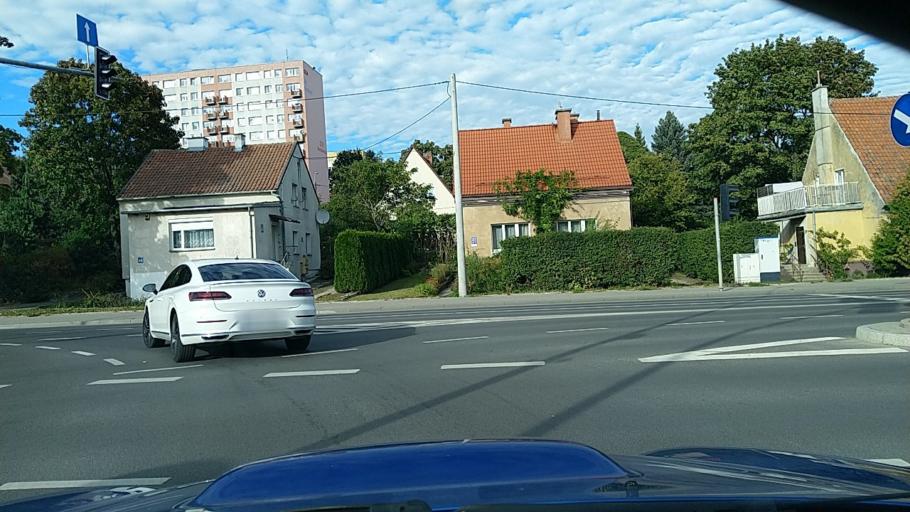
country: PL
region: Warmian-Masurian Voivodeship
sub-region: Powiat olsztynski
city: Olsztyn
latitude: 53.7745
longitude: 20.4946
